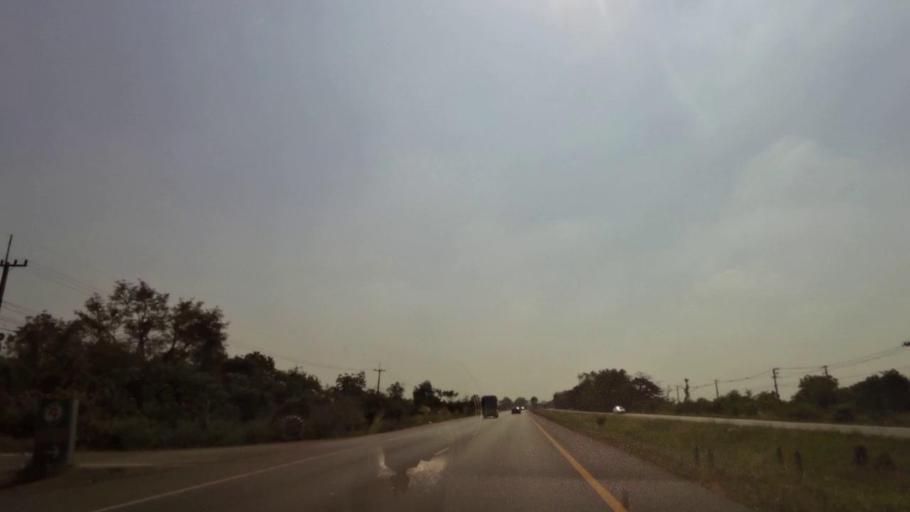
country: TH
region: Phichit
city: Wachira Barami
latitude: 16.4772
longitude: 100.1471
